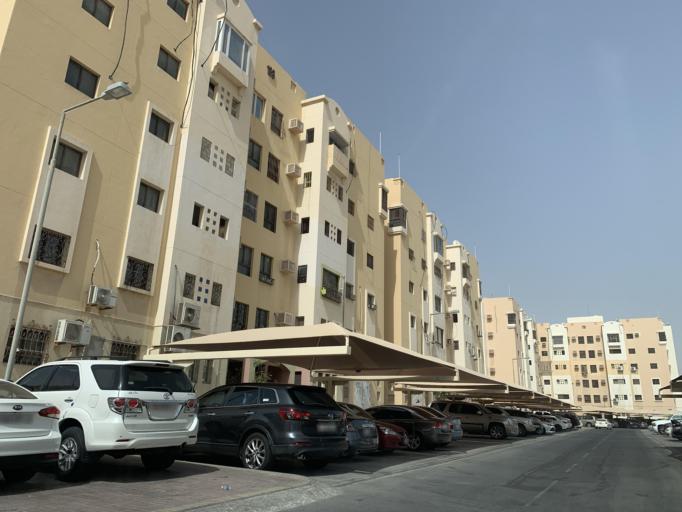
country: BH
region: Northern
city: Madinat `Isa
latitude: 26.1728
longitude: 50.5215
